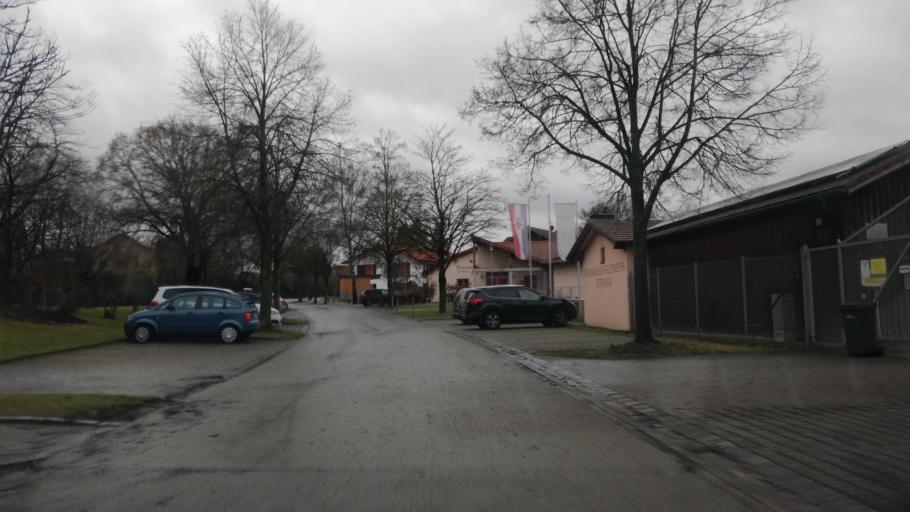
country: DE
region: Bavaria
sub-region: Upper Bavaria
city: Obertaufkirchen
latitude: 48.2607
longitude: 12.2841
